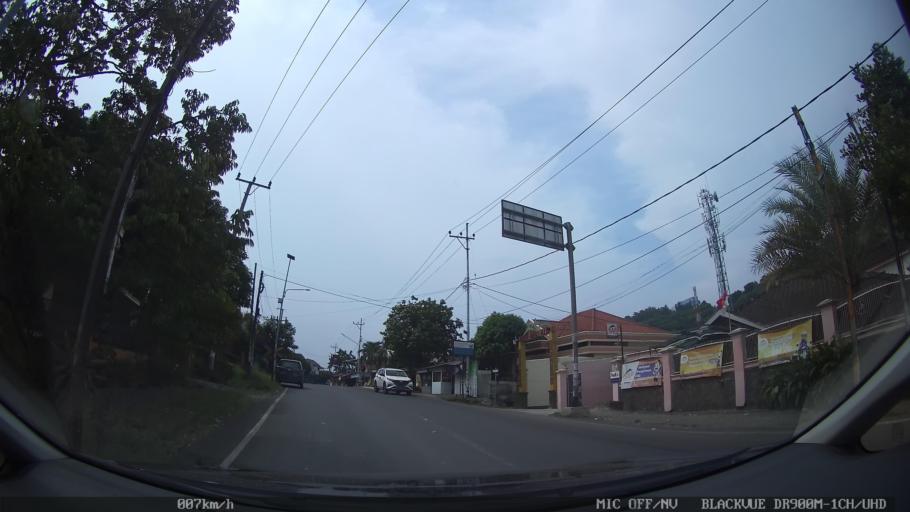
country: ID
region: Lampung
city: Bandarlampung
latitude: -5.4328
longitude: 105.2766
